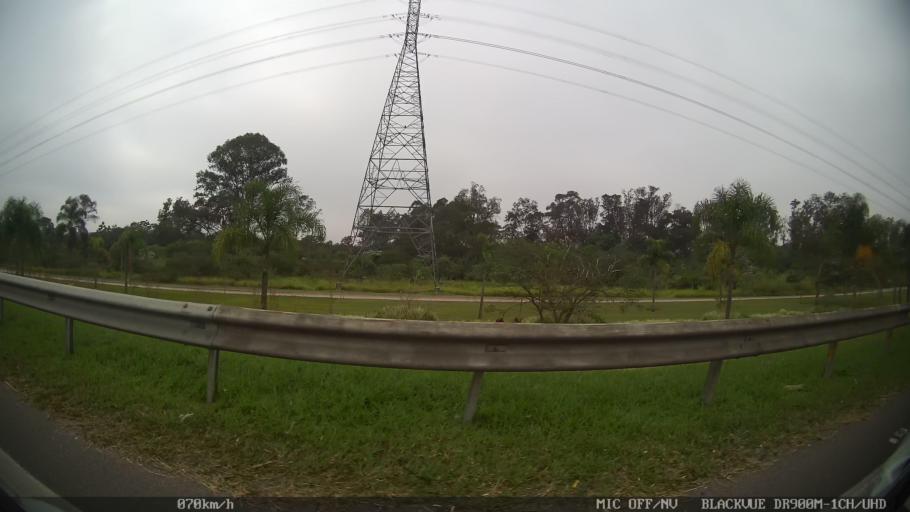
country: BR
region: Sao Paulo
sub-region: Guarulhos
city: Guarulhos
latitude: -23.4873
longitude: -46.5310
